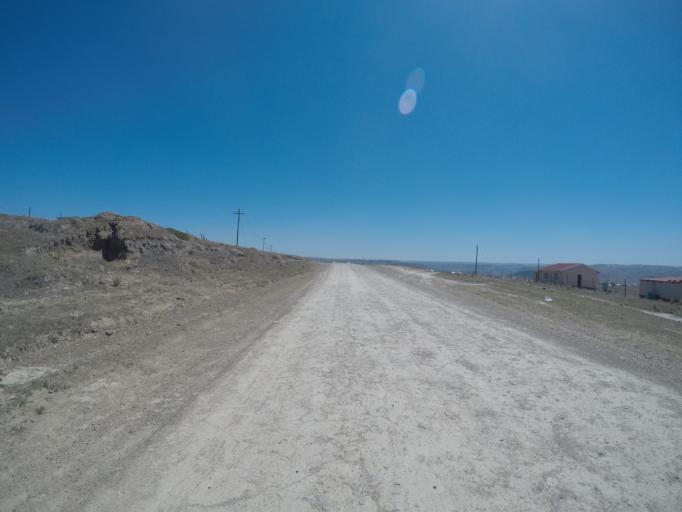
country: ZA
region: Eastern Cape
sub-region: OR Tambo District Municipality
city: Mthatha
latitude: -31.8921
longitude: 28.8837
